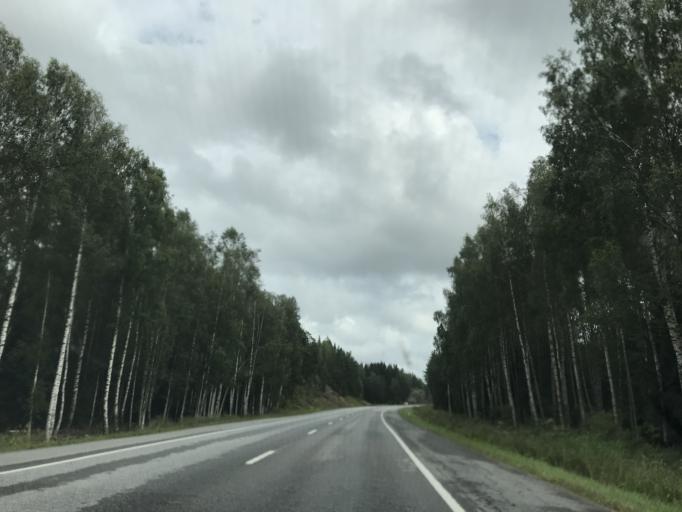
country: FI
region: Uusimaa
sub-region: Raaseporin
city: Karis
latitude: 60.0741
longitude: 23.7697
